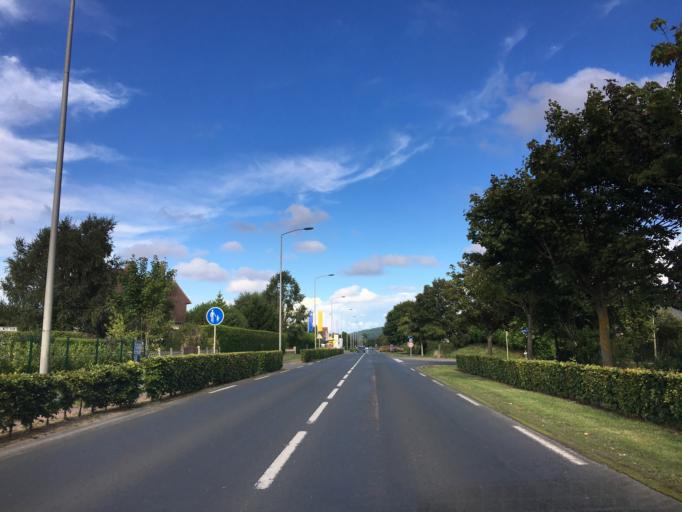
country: FR
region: Lower Normandy
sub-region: Departement du Calvados
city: Cabourg
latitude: 49.2837
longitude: -0.1335
